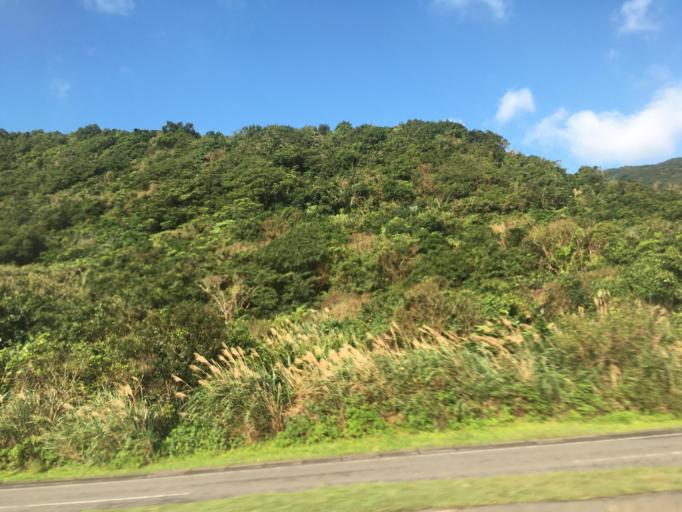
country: TW
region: Taiwan
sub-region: Yilan
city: Yilan
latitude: 24.9266
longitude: 121.8859
